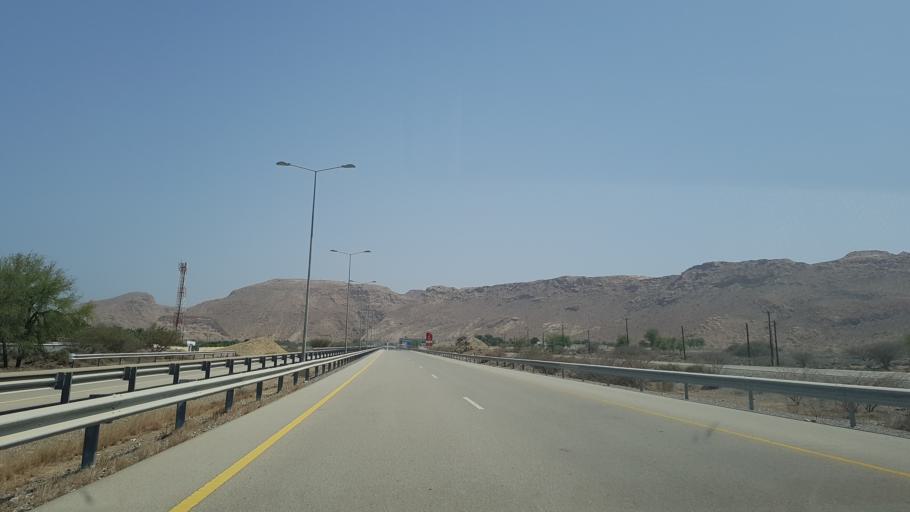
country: OM
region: Muhafazat Masqat
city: Muscat
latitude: 23.2001
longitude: 58.9492
